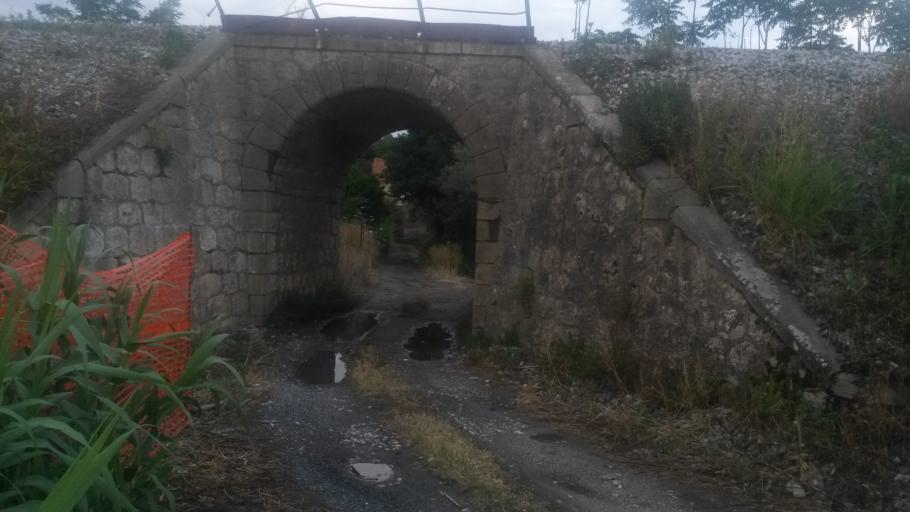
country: IT
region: Calabria
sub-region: Provincia di Catanzaro
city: Catanzaro
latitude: 38.8887
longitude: 16.6013
